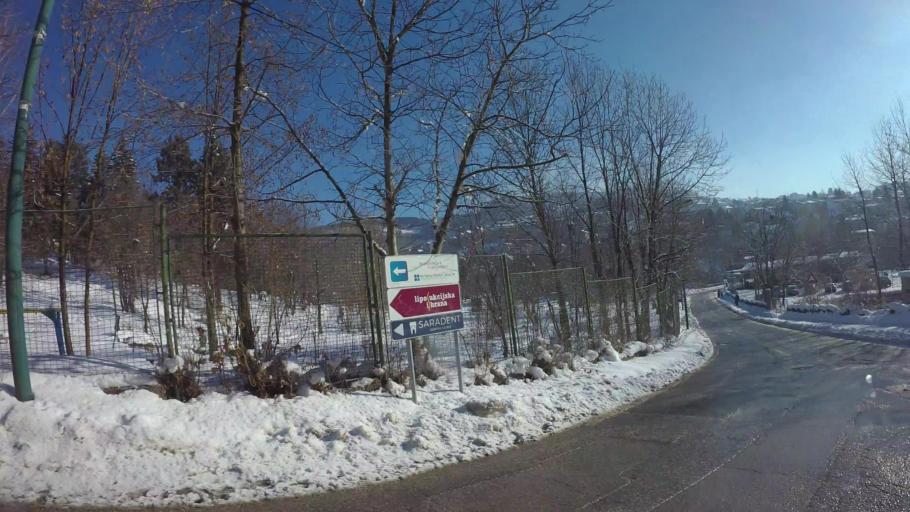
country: BA
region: Federation of Bosnia and Herzegovina
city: Kobilja Glava
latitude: 43.8777
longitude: 18.4106
